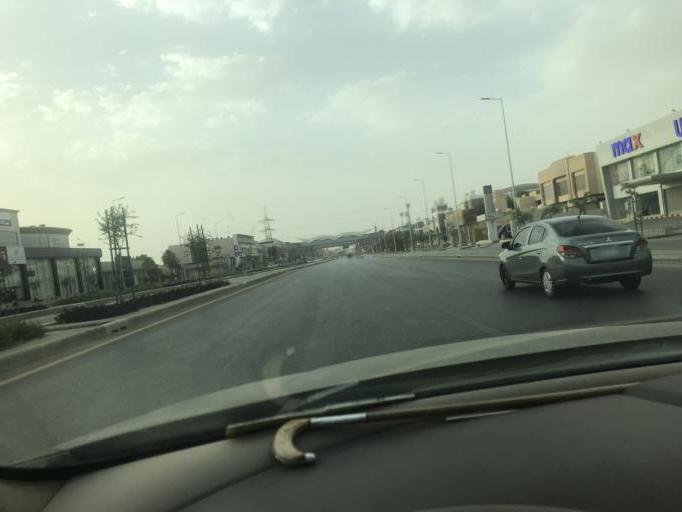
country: SA
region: Ar Riyad
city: Riyadh
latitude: 24.7810
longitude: 46.6630
